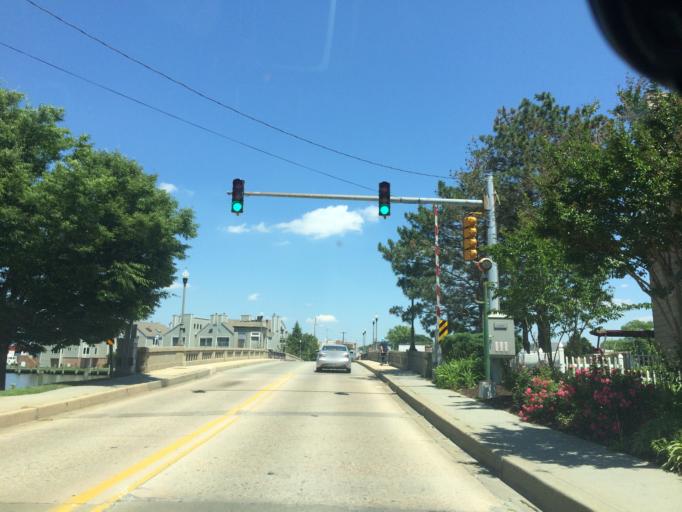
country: US
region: Maryland
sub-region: Dorchester County
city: Cambridge
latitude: 38.5702
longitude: -76.0746
